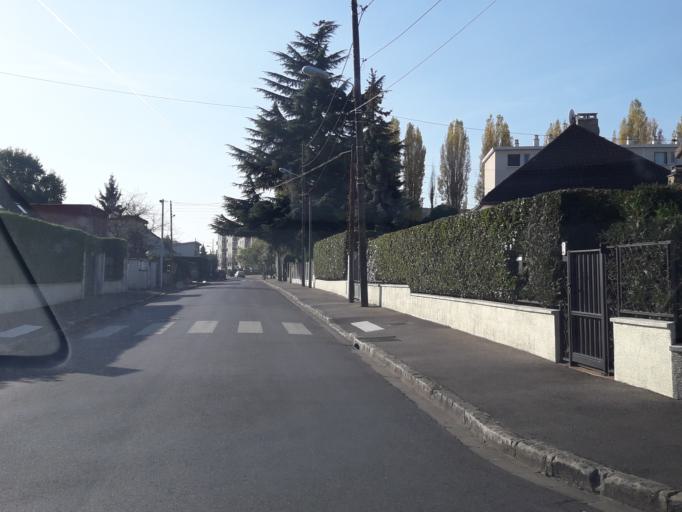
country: FR
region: Ile-de-France
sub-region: Departement de l'Essonne
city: Morsang-sur-Orge
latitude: 48.6558
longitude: 2.3582
